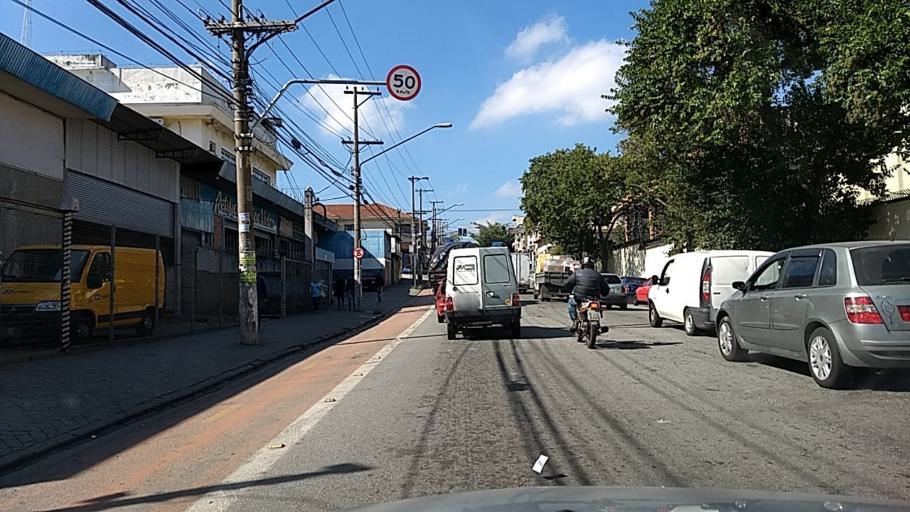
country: BR
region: Sao Paulo
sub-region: Sao Paulo
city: Sao Paulo
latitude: -23.5165
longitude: -46.5851
